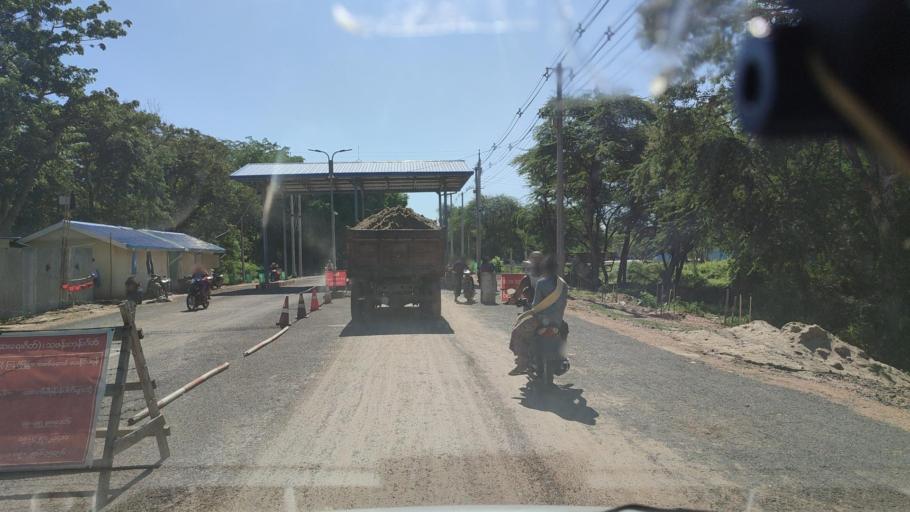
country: MM
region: Magway
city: Taungdwingyi
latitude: 19.9988
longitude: 95.5226
